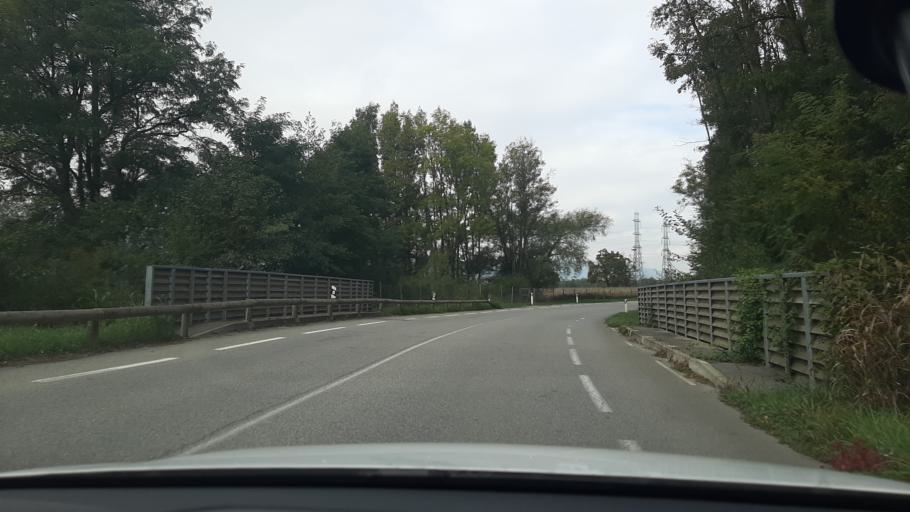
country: FR
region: Rhone-Alpes
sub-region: Departement de la Savoie
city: Montmelian
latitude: 45.4625
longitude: 6.0471
